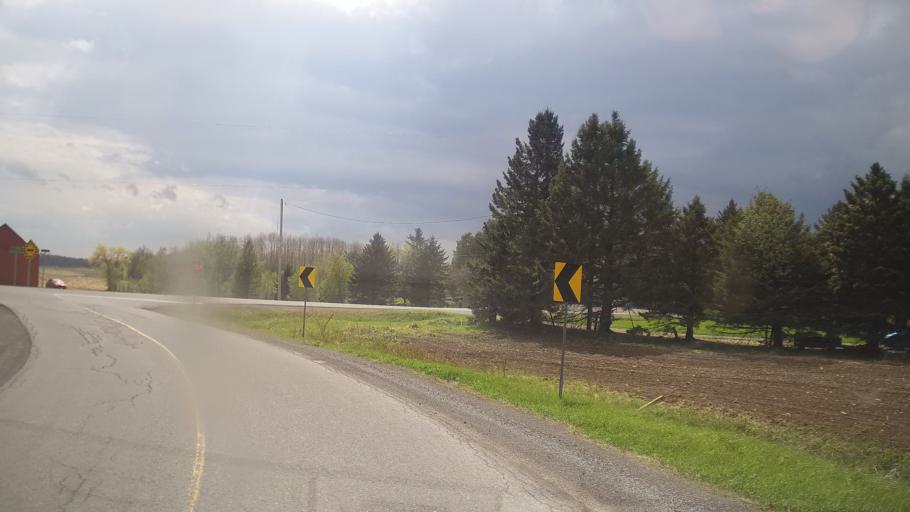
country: CA
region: Ontario
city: Hawkesbury
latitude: 45.5188
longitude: -74.5703
